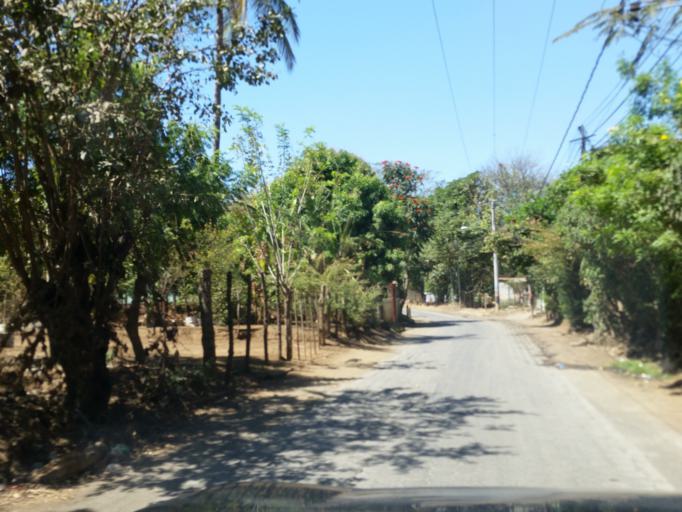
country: NI
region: Managua
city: Managua
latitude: 12.0822
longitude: -86.2374
